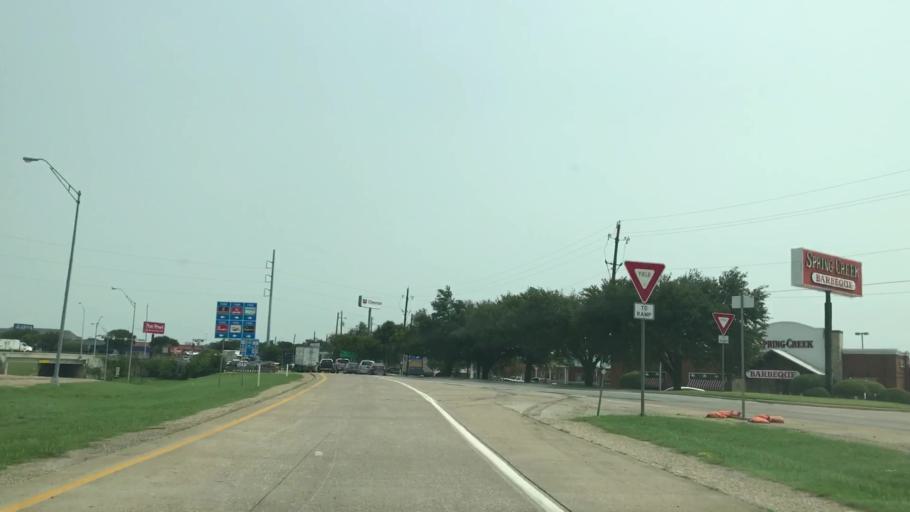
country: US
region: Texas
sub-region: Dallas County
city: Irving
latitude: 32.8360
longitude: -96.9958
